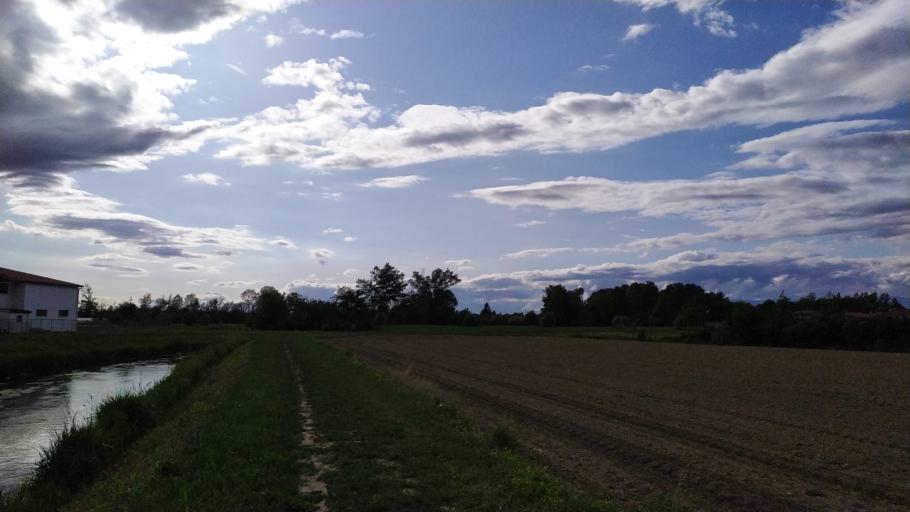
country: IT
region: Veneto
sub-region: Provincia di Padova
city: Villa del Conte
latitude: 45.5894
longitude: 11.8507
